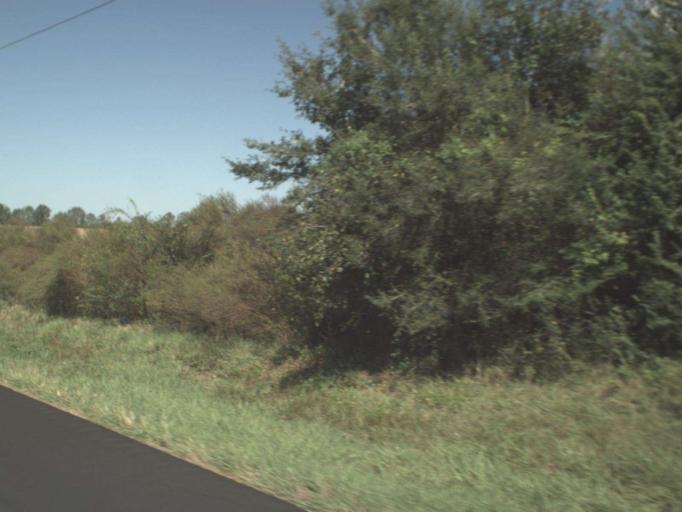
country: US
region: Alabama
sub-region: Covington County
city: Florala
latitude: 30.8726
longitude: -86.2590
